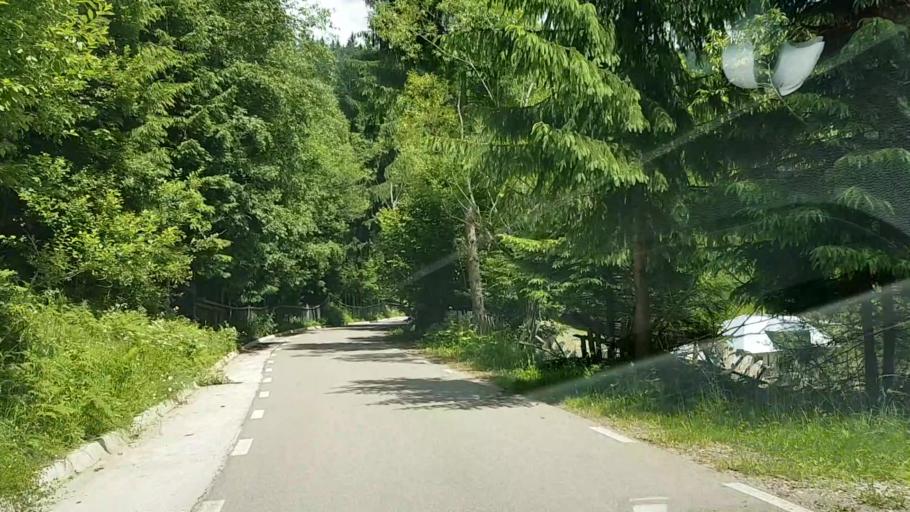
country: RO
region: Suceava
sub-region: Comuna Crucea
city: Crucea
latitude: 47.4233
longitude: 25.5774
